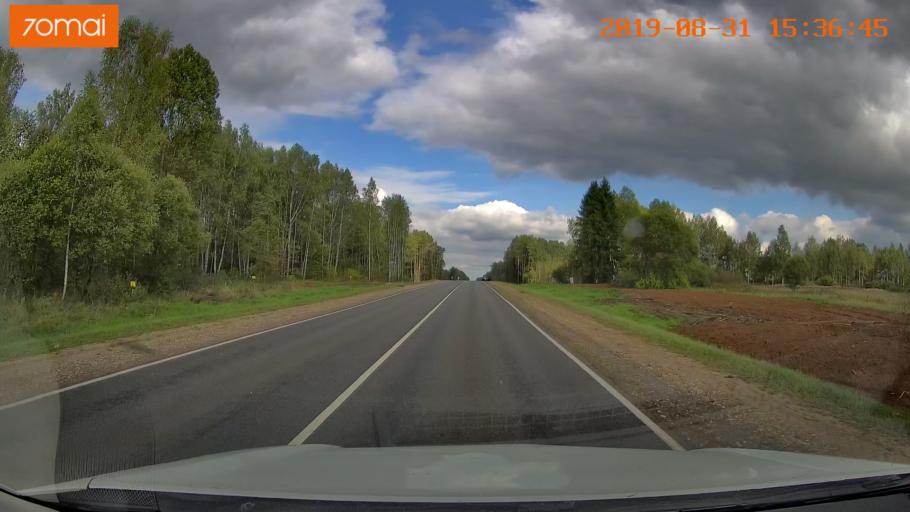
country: RU
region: Kaluga
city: Mosal'sk
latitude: 54.6133
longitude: 34.7666
